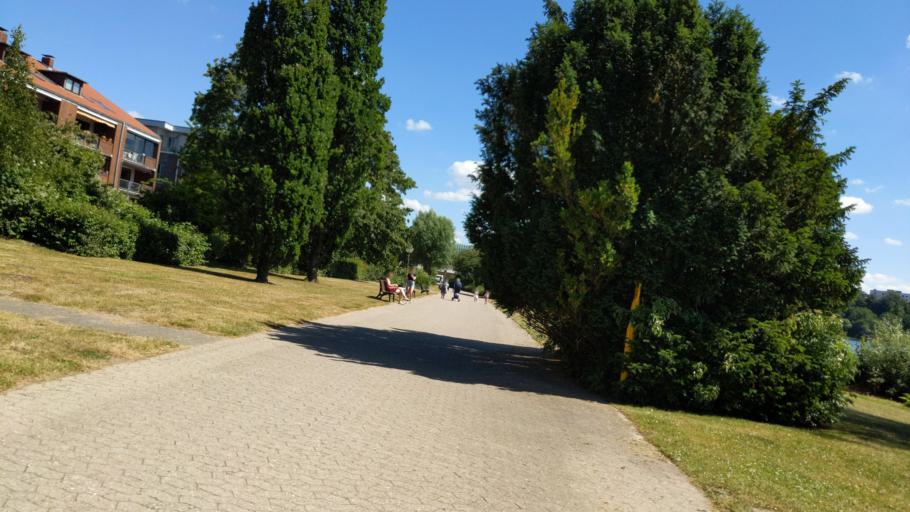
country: DE
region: Schleswig-Holstein
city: Ratzeburg
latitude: 53.6961
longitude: 10.7733
